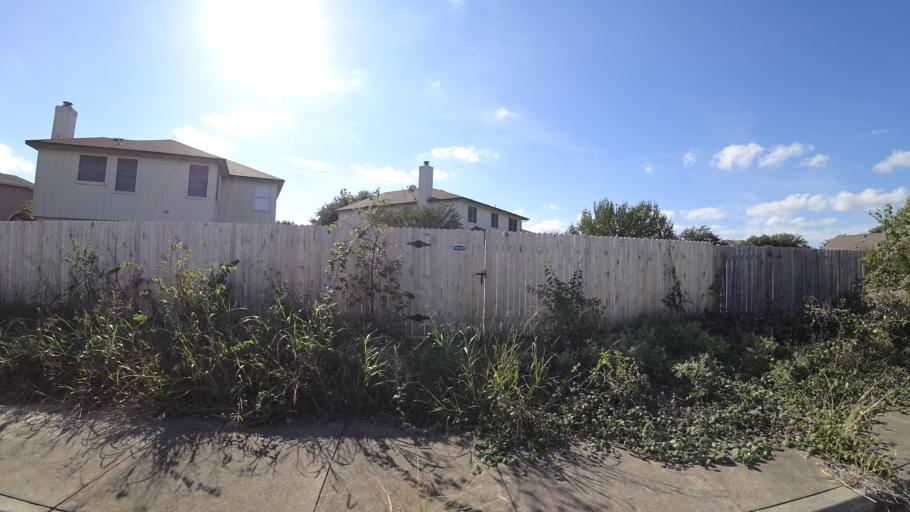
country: US
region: Texas
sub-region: Travis County
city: Wells Branch
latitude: 30.4598
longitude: -97.6800
